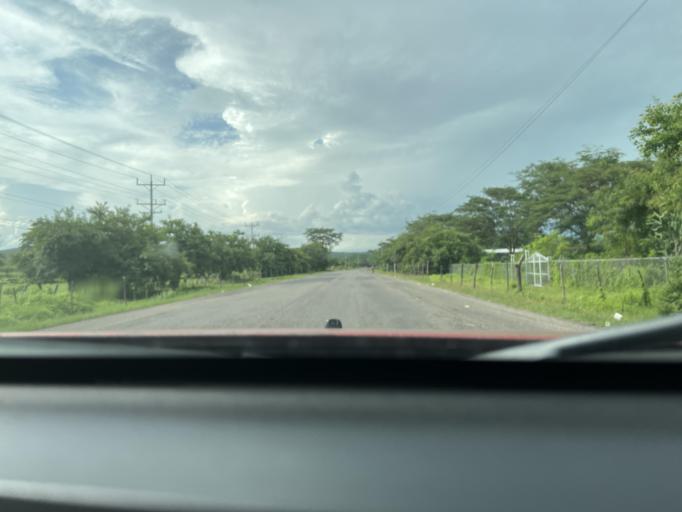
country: SV
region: La Union
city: La Union
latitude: 13.3749
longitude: -87.9090
